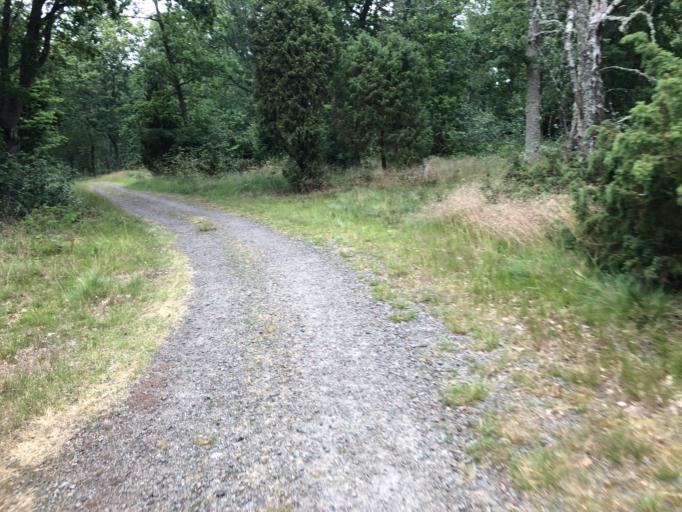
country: SE
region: Kalmar
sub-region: Kalmar Kommun
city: Kalmar
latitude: 56.6402
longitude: 16.3220
